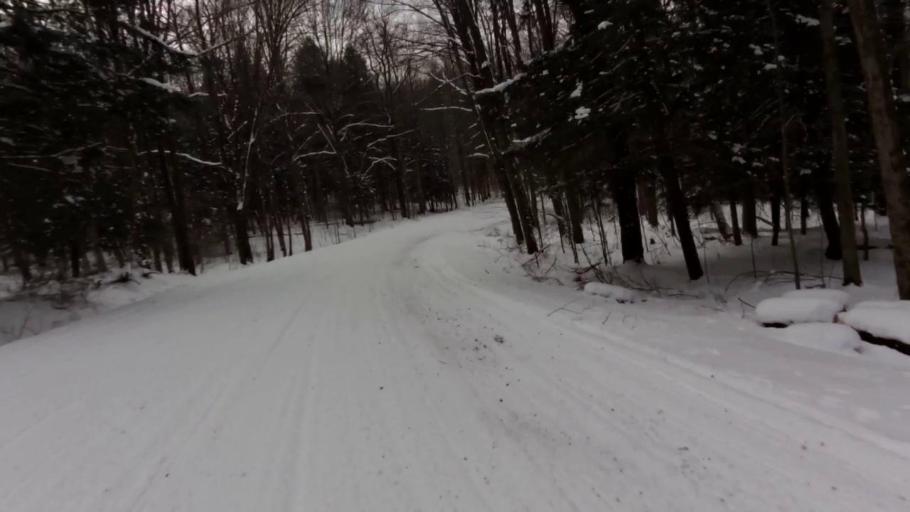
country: US
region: New York
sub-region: Cattaraugus County
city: Salamanca
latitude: 42.0368
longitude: -78.7869
